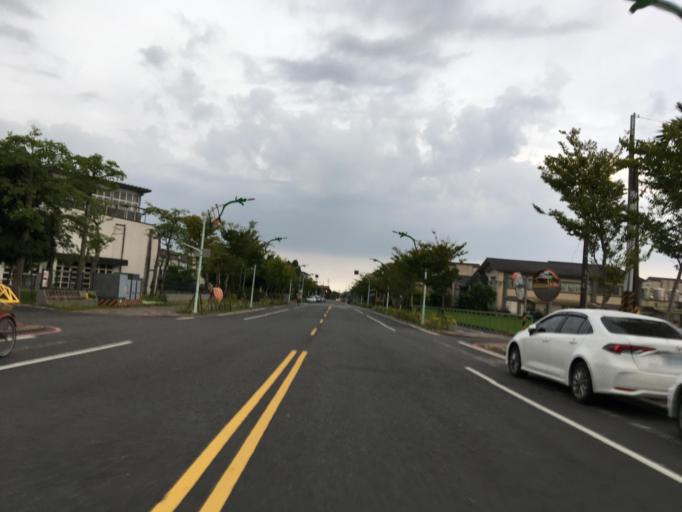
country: TW
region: Taiwan
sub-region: Yilan
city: Yilan
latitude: 24.6628
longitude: 121.7633
